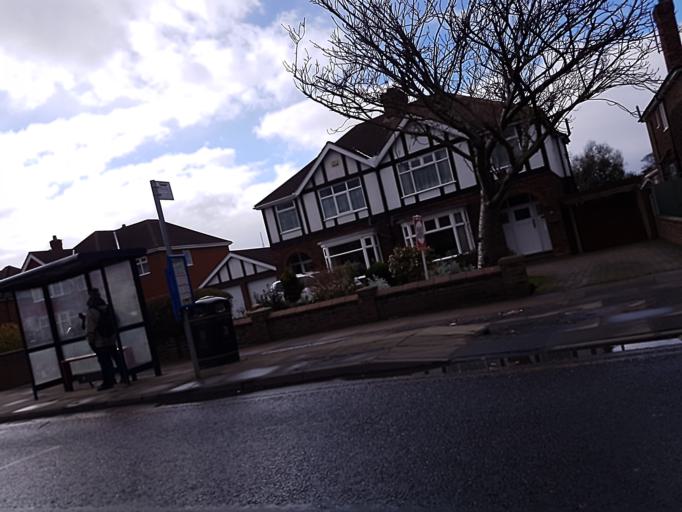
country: GB
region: England
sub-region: North East Lincolnshire
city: Grimbsy
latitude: 53.5579
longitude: -0.0916
